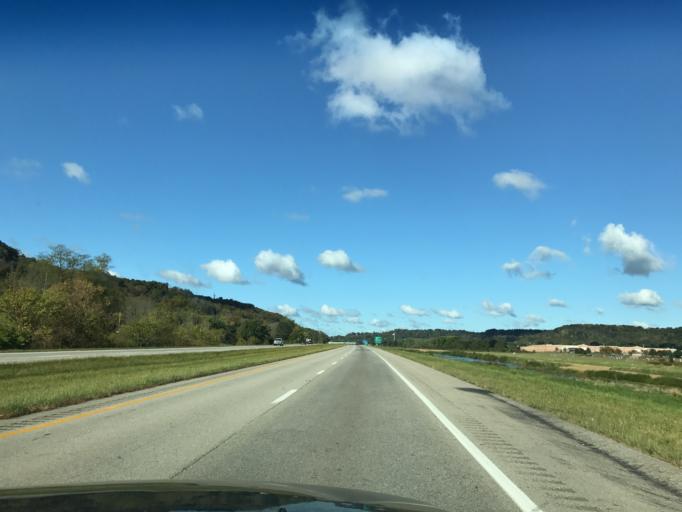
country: US
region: Ohio
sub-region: Athens County
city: Athens
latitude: 39.3321
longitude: -82.0574
